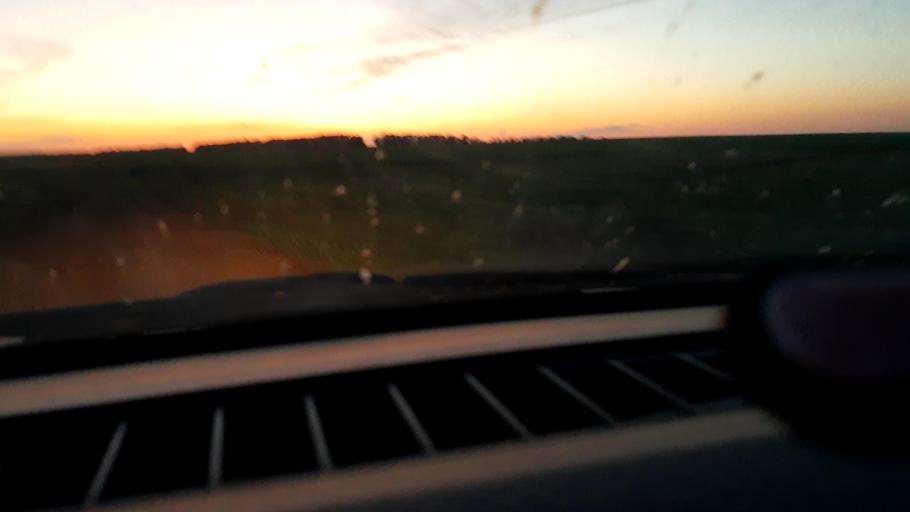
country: RU
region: Bashkortostan
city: Asanovo
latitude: 54.8534
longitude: 55.5850
